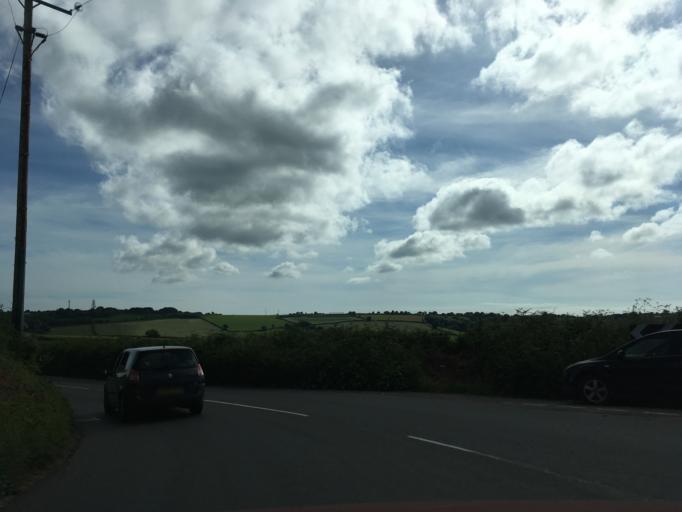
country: GB
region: England
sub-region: Devon
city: Totnes
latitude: 50.3657
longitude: -3.7134
